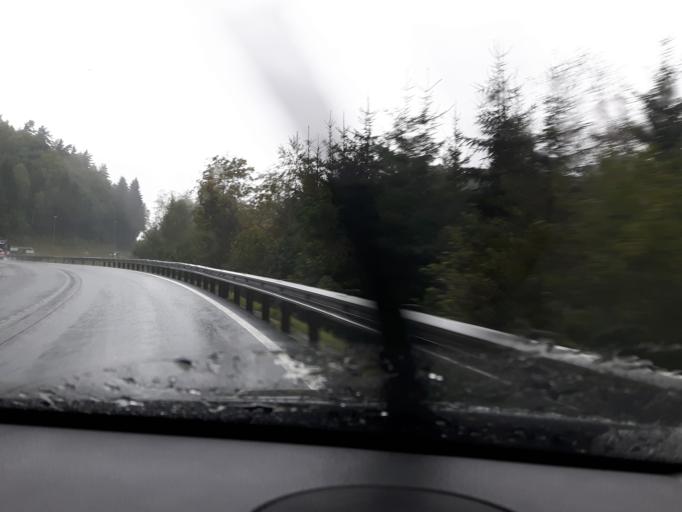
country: NO
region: Vest-Agder
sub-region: Mandal
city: Mandal
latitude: 58.0489
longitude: 7.3947
